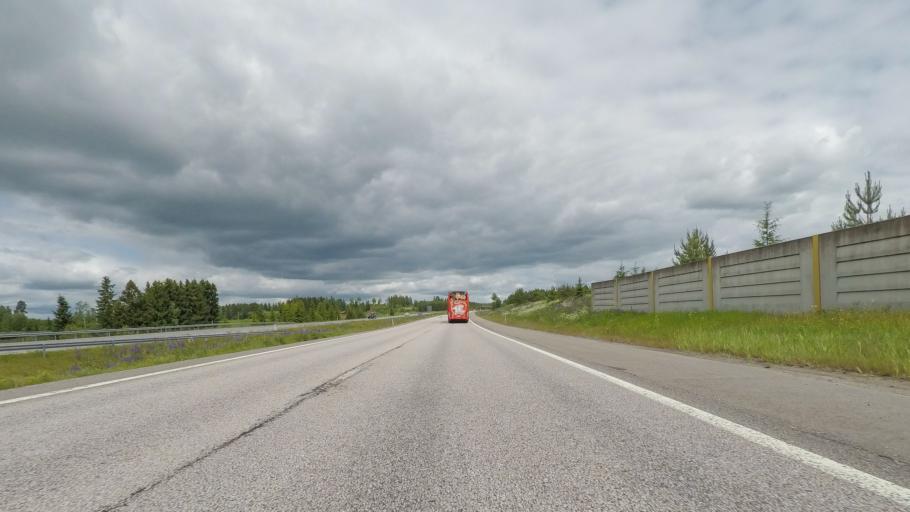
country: FI
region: Uusimaa
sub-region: Helsinki
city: Jaervenpaeae
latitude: 60.5116
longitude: 25.1411
